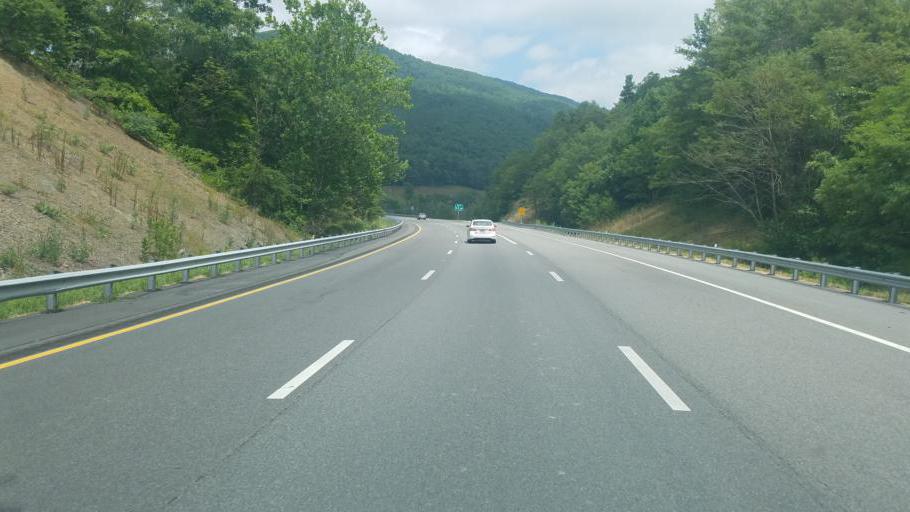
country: US
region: Virginia
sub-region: Bland County
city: Bland
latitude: 37.2125
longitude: -81.0931
